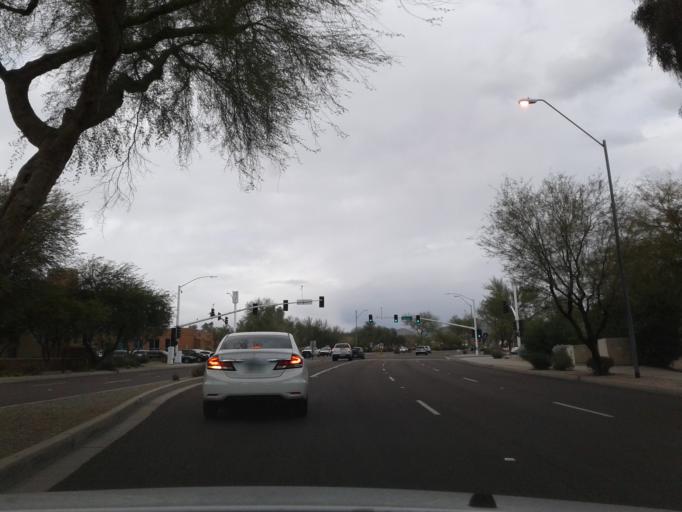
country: US
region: Arizona
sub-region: Maricopa County
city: Paradise Valley
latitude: 33.6178
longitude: -111.8783
